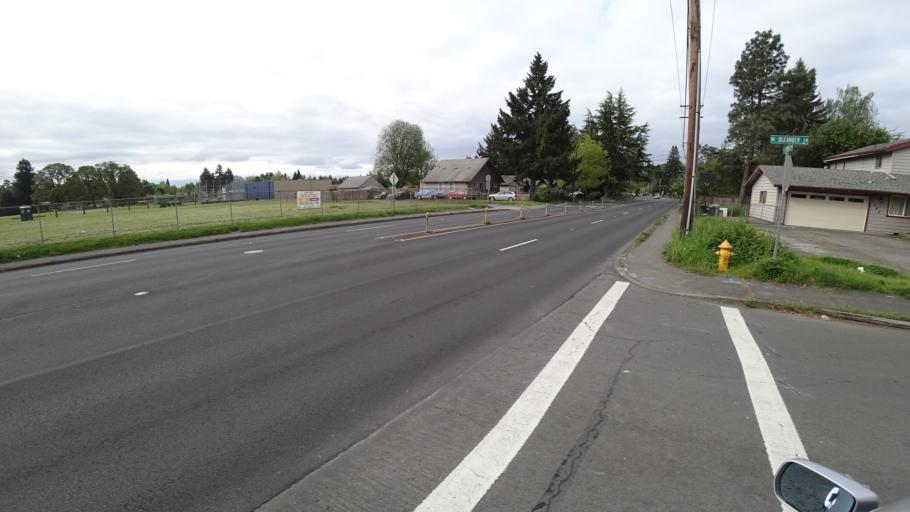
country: US
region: Oregon
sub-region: Washington County
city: Hillsboro
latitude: 45.5302
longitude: -122.9667
